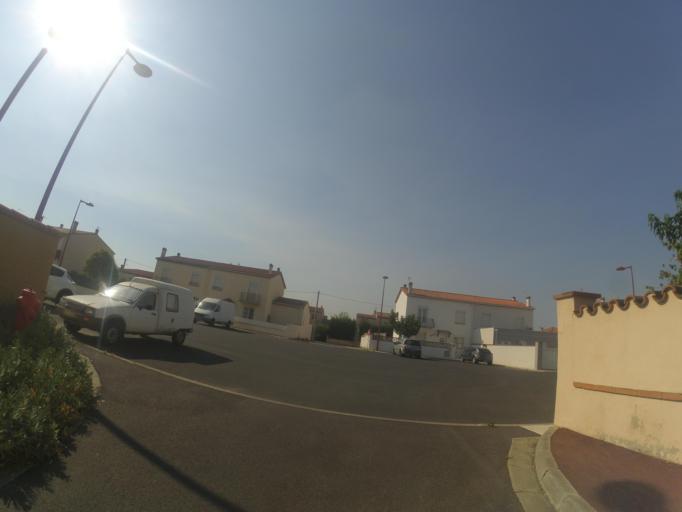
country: FR
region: Languedoc-Roussillon
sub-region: Departement des Pyrenees-Orientales
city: Toulouges
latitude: 42.6681
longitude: 2.8307
